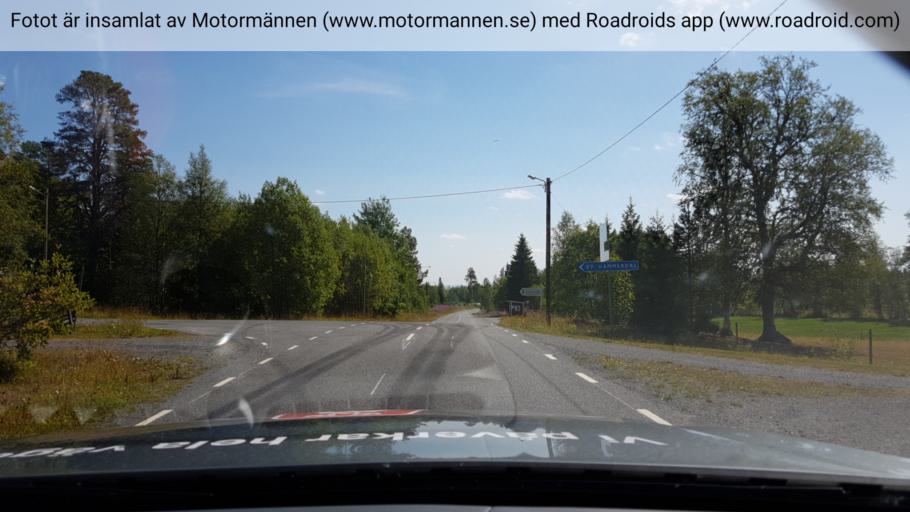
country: SE
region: Jaemtland
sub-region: OEstersunds Kommun
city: Lit
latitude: 63.3715
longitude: 15.1845
